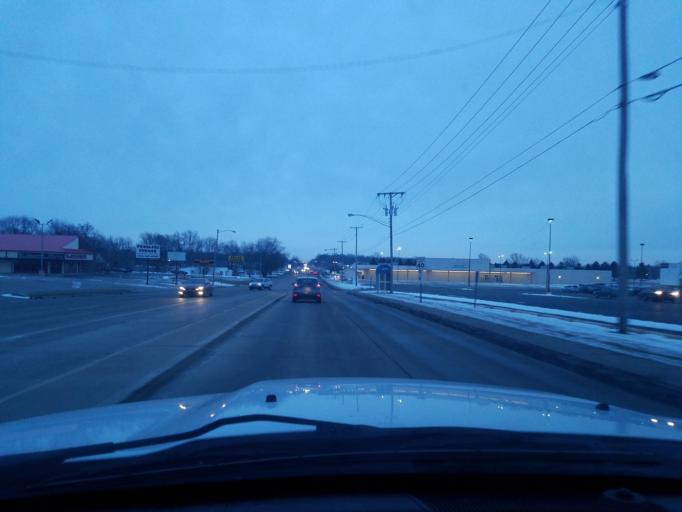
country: US
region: Indiana
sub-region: Delaware County
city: Muncie
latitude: 40.2190
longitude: -85.3729
